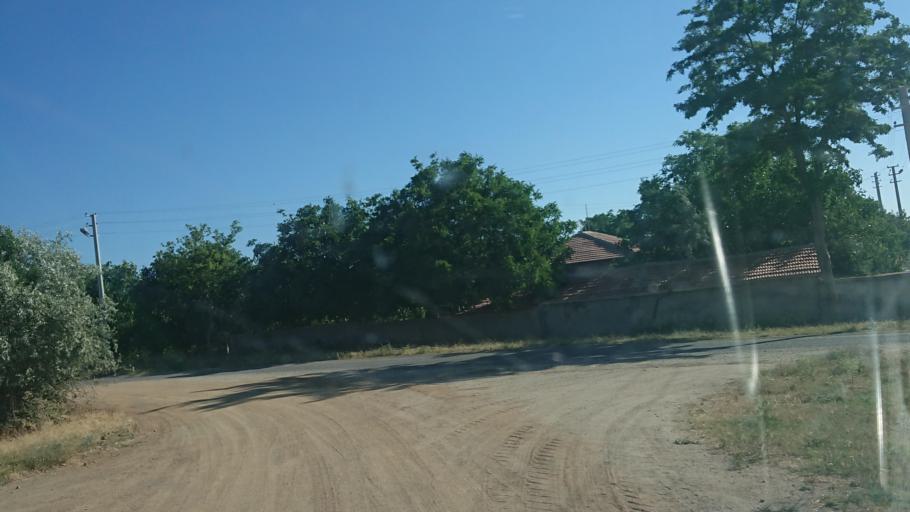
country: TR
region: Aksaray
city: Agacoren
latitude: 38.8769
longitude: 33.9523
